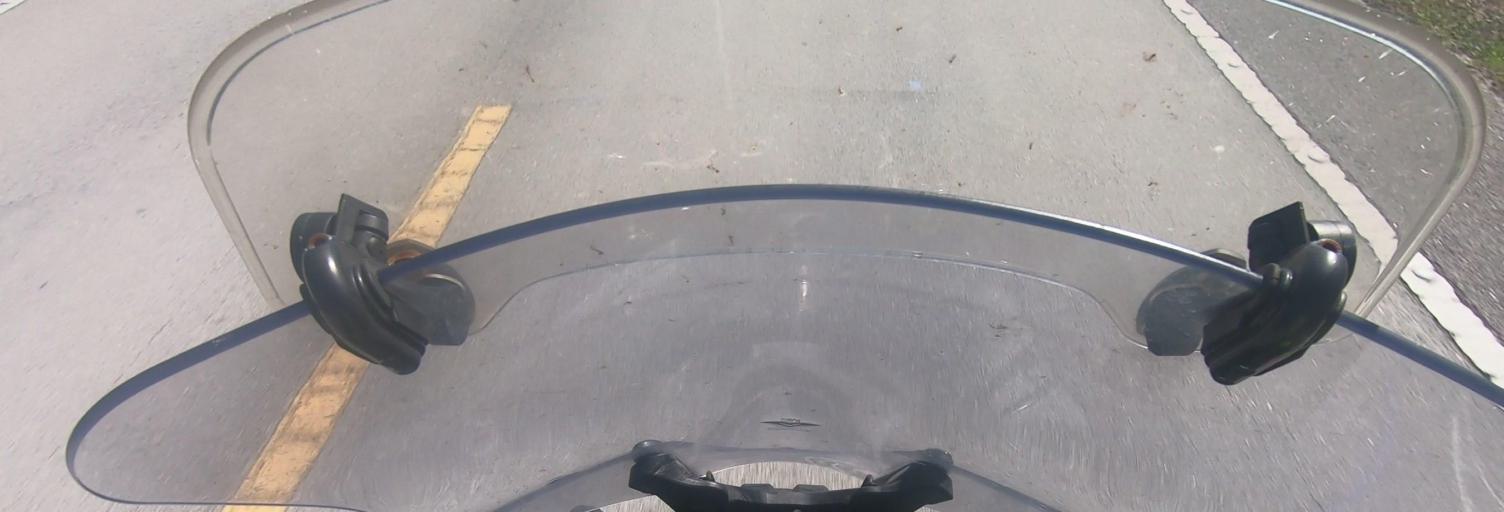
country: US
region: Florida
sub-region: Collier County
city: Marco
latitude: 25.8717
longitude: -81.1741
